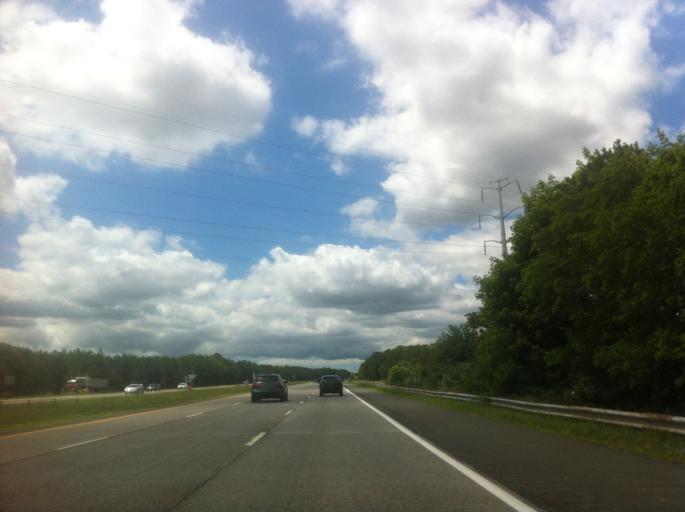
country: US
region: New York
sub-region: Suffolk County
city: Calverton
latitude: 40.9037
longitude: -72.7411
